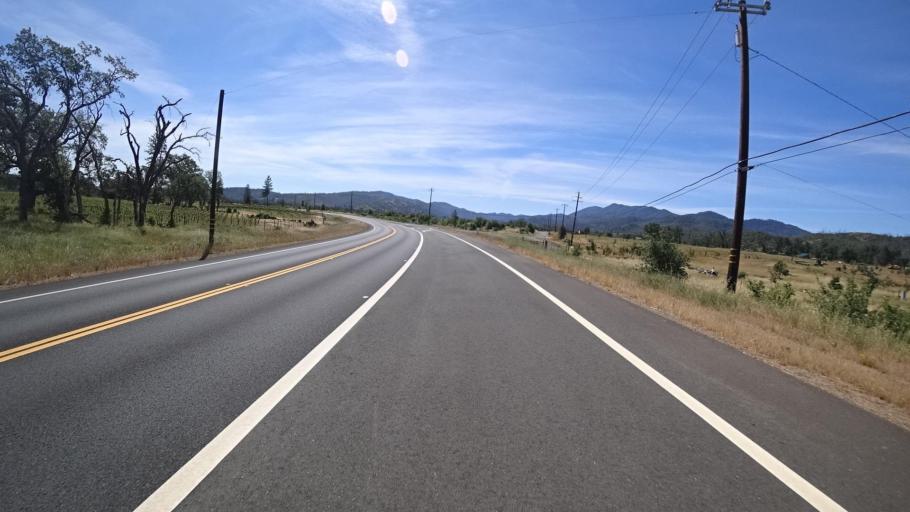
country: US
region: California
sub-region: Lake County
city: Middletown
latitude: 38.7602
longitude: -122.6418
